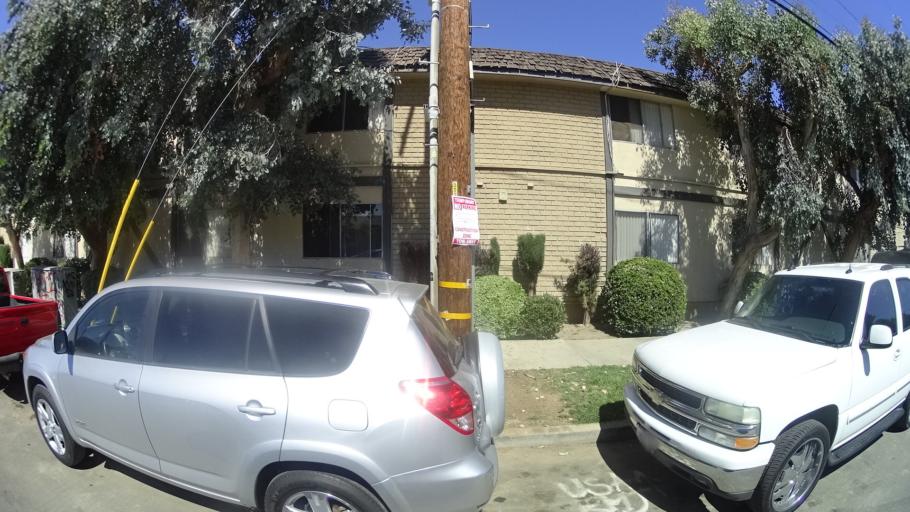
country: US
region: California
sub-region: Los Angeles County
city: Van Nuys
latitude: 34.1935
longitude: -118.4814
